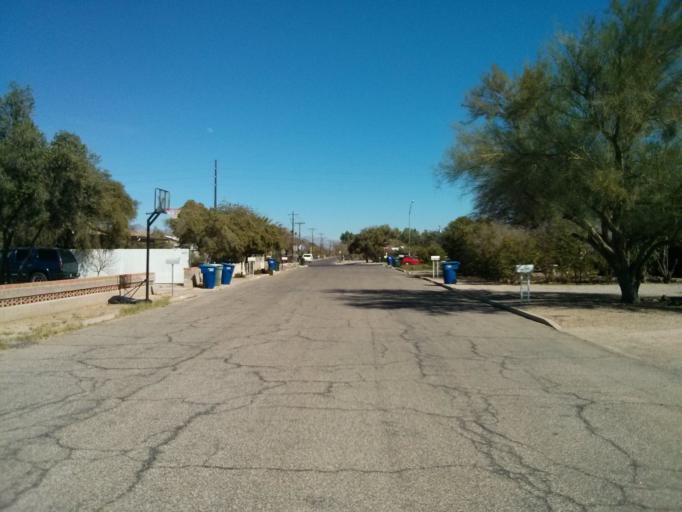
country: US
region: Arizona
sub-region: Pima County
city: Catalina Foothills
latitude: 32.2758
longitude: -110.9535
